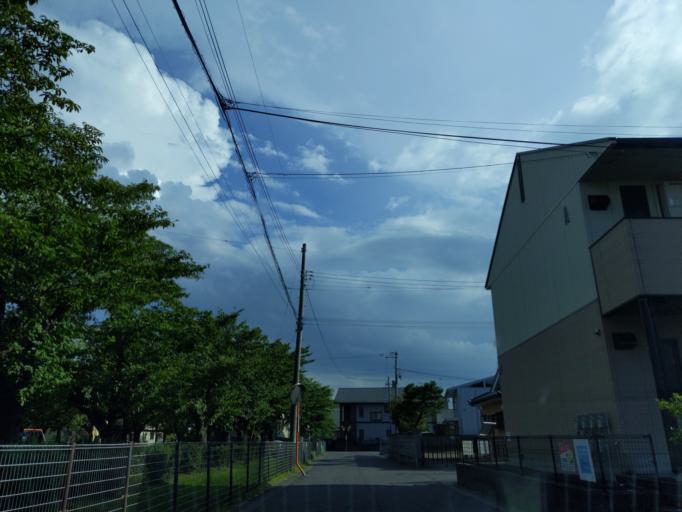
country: JP
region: Fukushima
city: Koriyama
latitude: 37.3896
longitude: 140.3309
